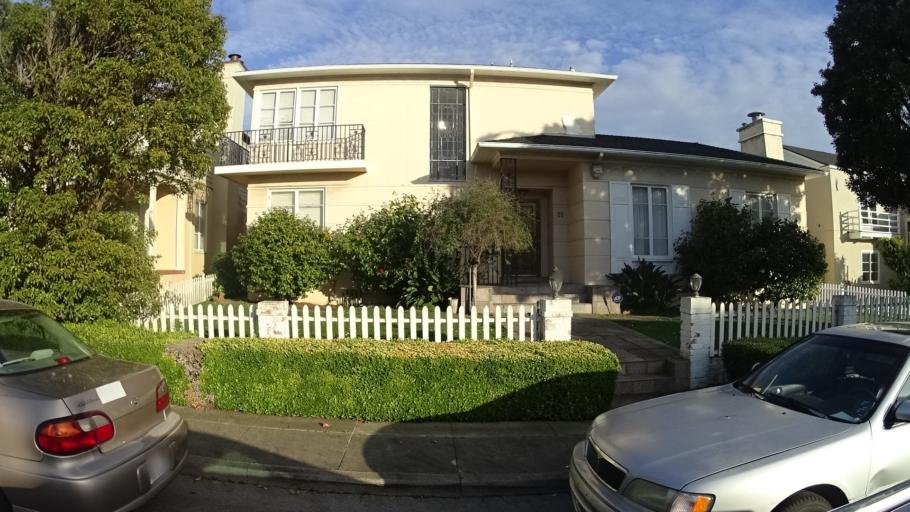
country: US
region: California
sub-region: San Mateo County
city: Daly City
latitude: 37.7279
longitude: -122.4732
